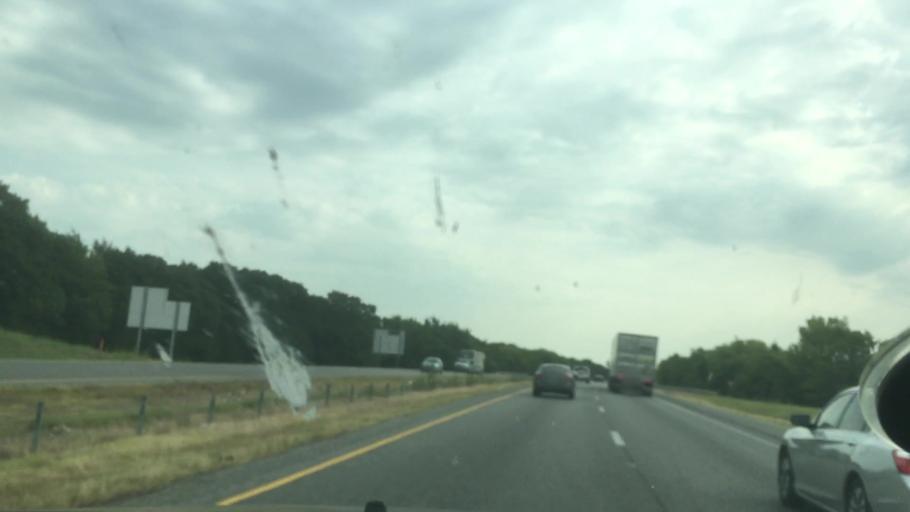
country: US
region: Oklahoma
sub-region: Bryan County
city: Colbert
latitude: 33.8329
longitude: -96.5256
